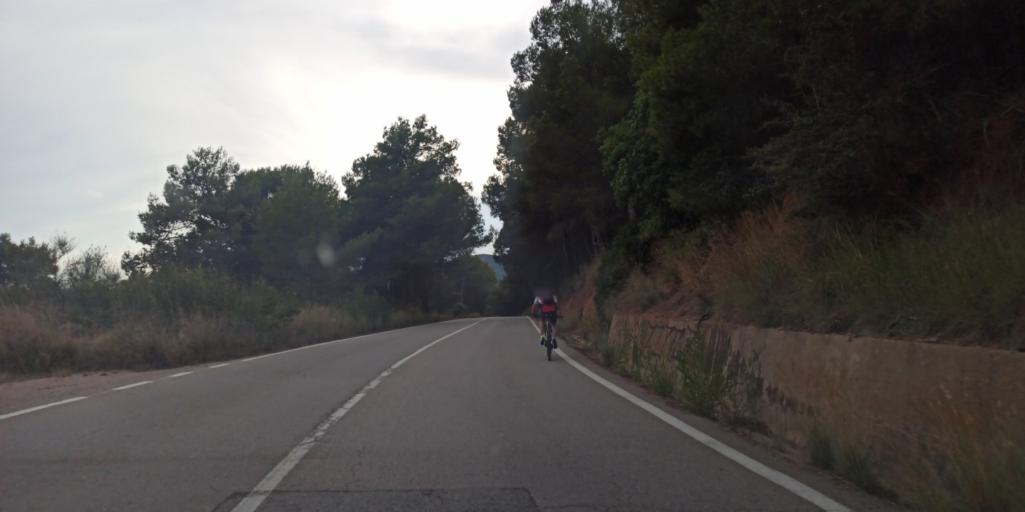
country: ES
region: Catalonia
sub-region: Provincia de Barcelona
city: Gava
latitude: 41.2999
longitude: 1.9879
